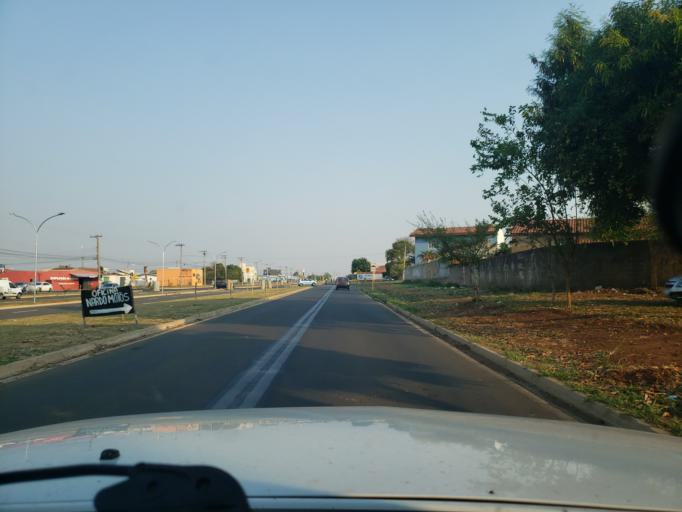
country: BR
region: Sao Paulo
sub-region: Moji-Guacu
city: Mogi-Gaucu
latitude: -22.3350
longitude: -46.9460
